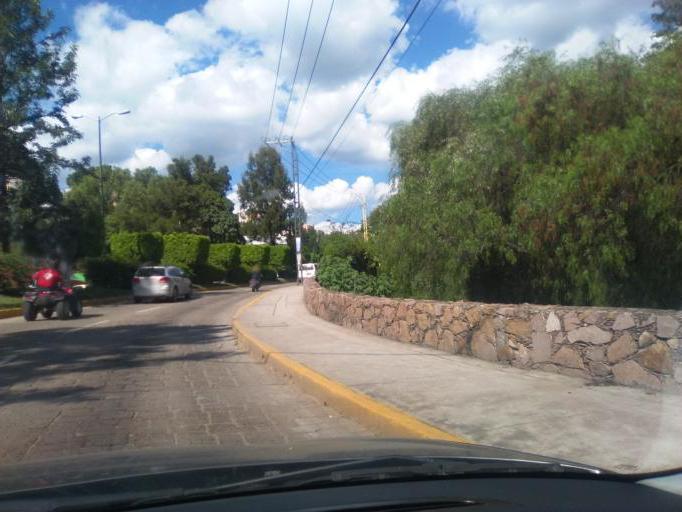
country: MX
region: Guanajuato
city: Guanajuato
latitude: 21.0130
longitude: -101.2676
